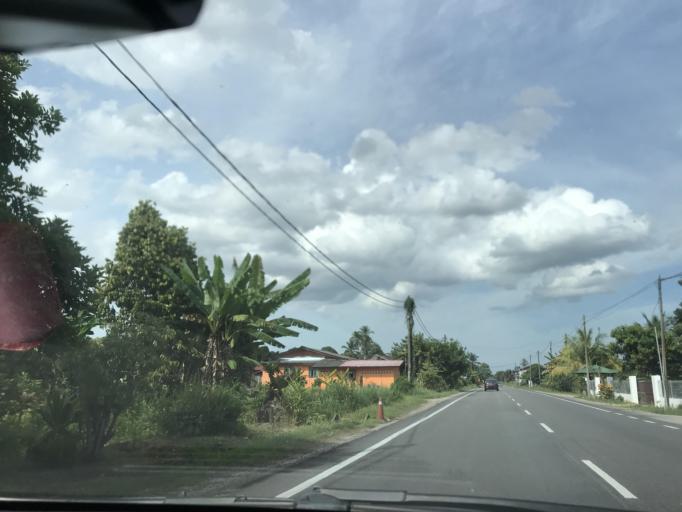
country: MY
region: Kelantan
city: Kampung Lemal
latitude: 6.0348
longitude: 102.1738
